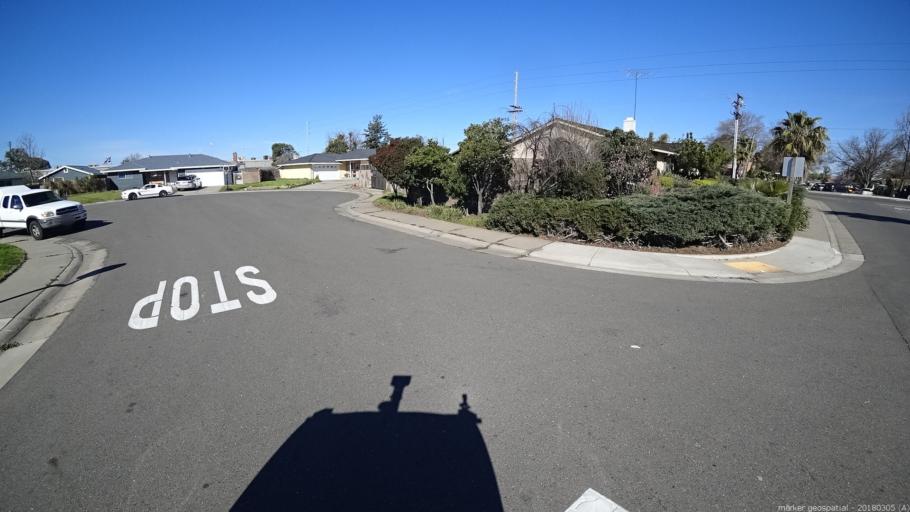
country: US
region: California
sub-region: Sacramento County
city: Florin
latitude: 38.4954
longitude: -121.4242
